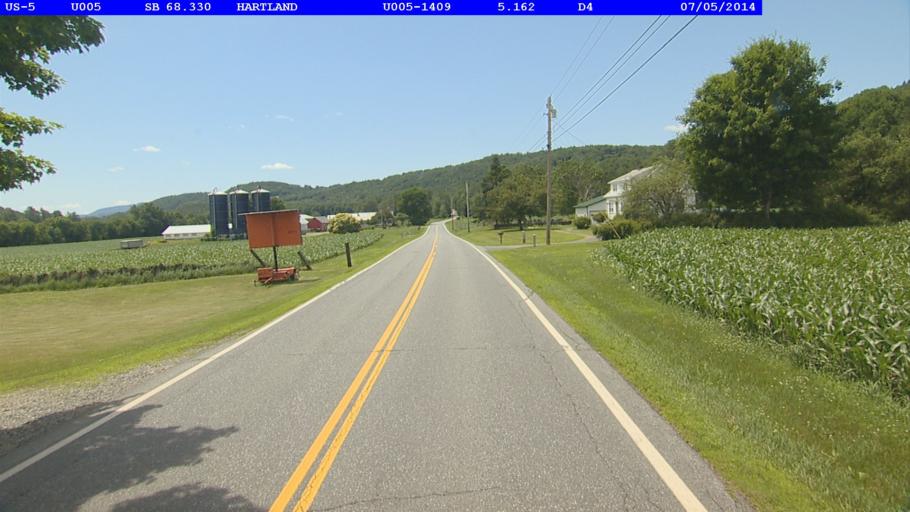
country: US
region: Vermont
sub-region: Windsor County
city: White River Junction
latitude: 43.5827
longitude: -72.3731
